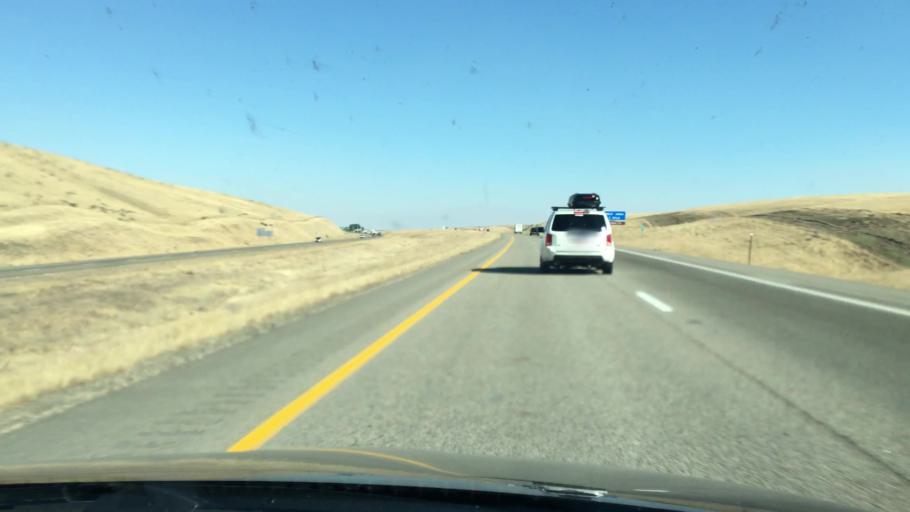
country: US
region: Idaho
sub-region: Ada County
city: Boise
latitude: 43.4912
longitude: -116.1262
